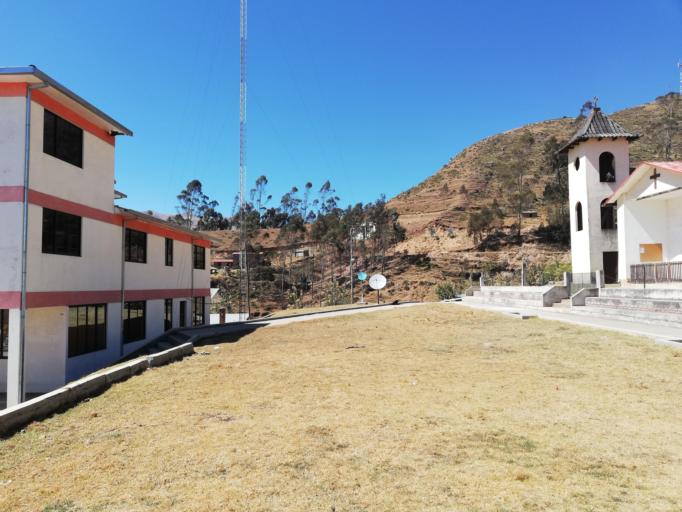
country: BO
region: Cochabamba
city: Colchani
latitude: -16.7996
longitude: -66.6683
